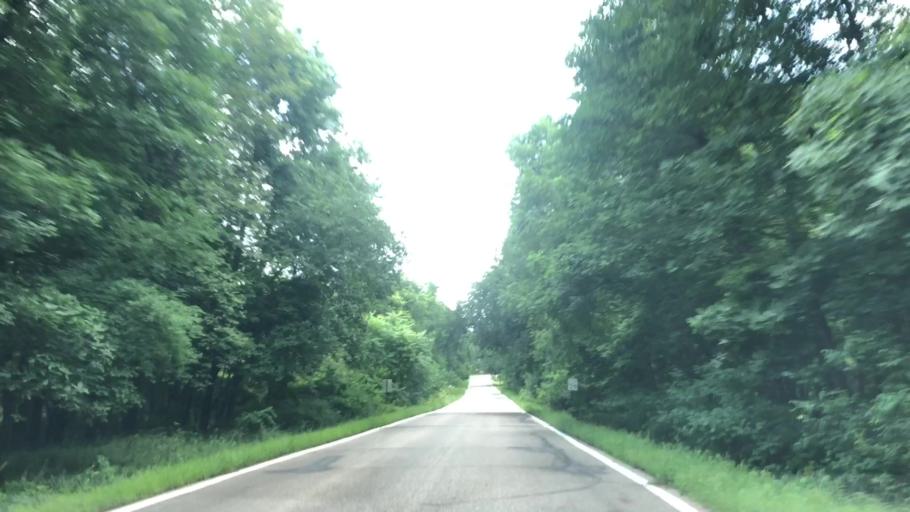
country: US
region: Iowa
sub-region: Marshall County
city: Marshalltown
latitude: 42.0256
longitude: -92.9459
